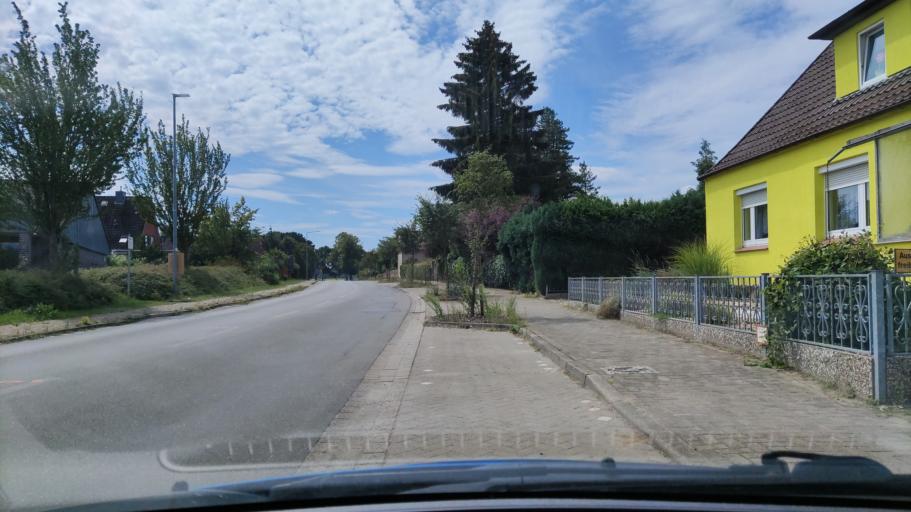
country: DE
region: Lower Saxony
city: Clenze
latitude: 52.9304
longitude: 10.9513
